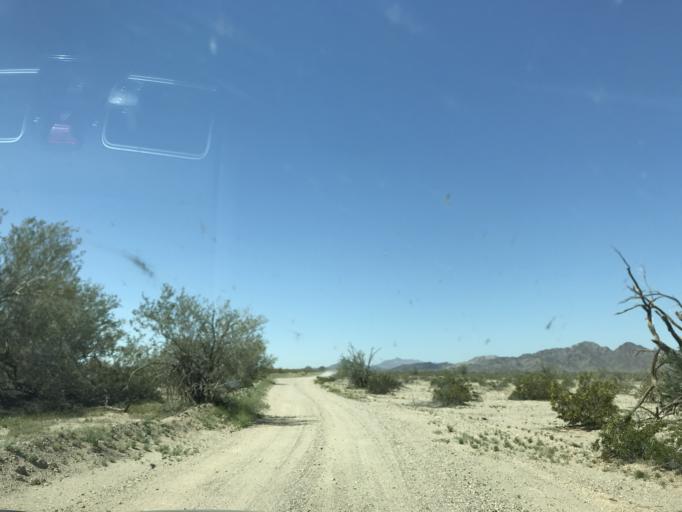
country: US
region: California
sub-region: Riverside County
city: Mesa Verde
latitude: 33.4847
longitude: -114.9102
